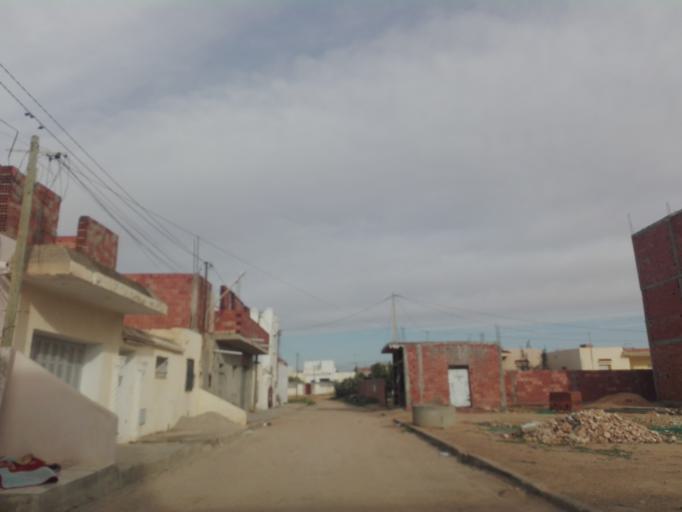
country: TN
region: Safaqis
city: Sfax
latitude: 34.7428
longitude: 10.5232
